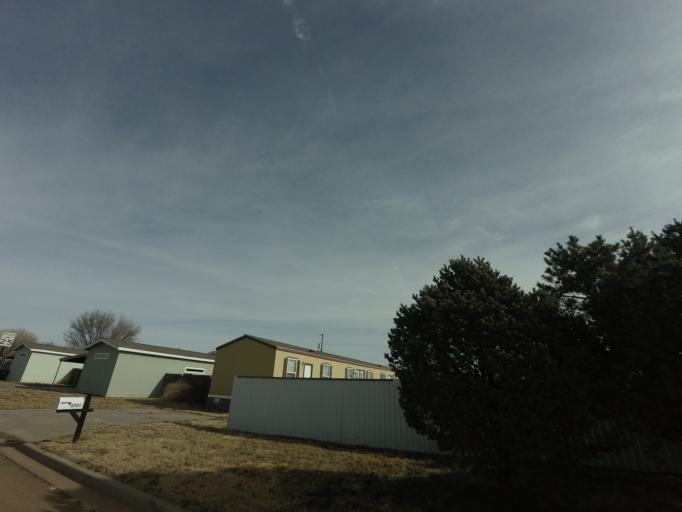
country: US
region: New Mexico
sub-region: Curry County
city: Clovis
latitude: 34.4049
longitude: -103.2467
